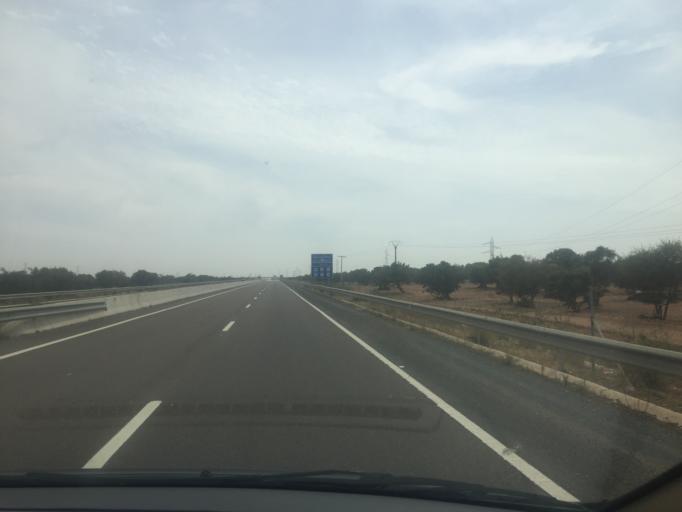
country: MA
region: Souss-Massa-Draa
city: Oulad Teima
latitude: 30.4668
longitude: -9.3550
